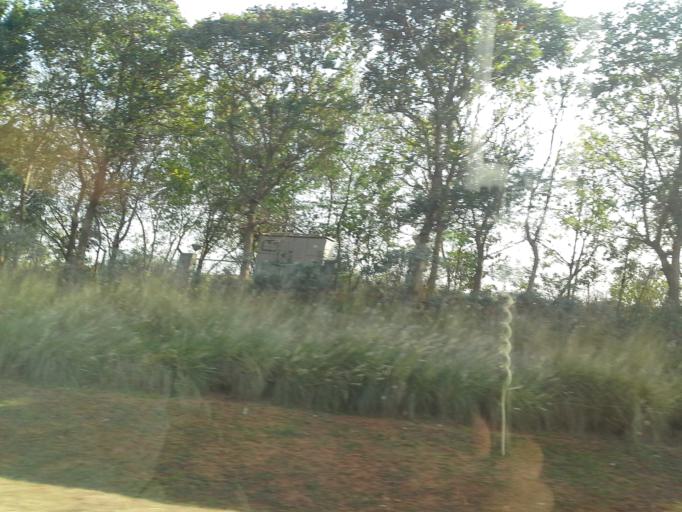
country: IN
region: Telangana
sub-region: Rangareddi
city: Balapur
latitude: 17.2446
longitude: 78.3952
